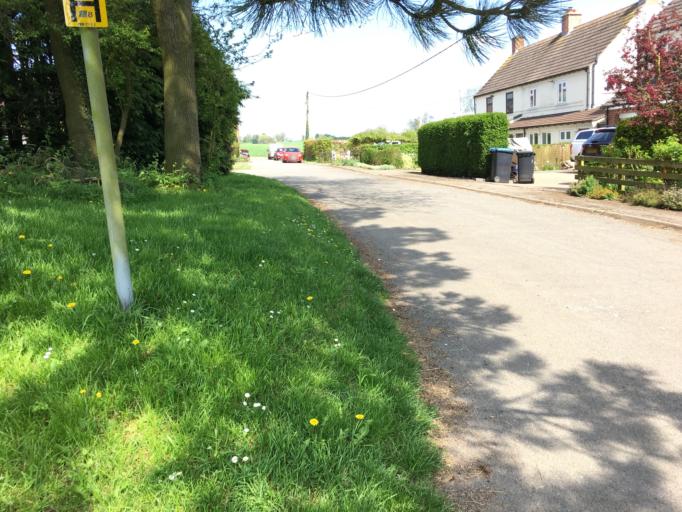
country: GB
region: England
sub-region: Leicestershire
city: Houghton on the Hill
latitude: 52.6011
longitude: -0.9731
